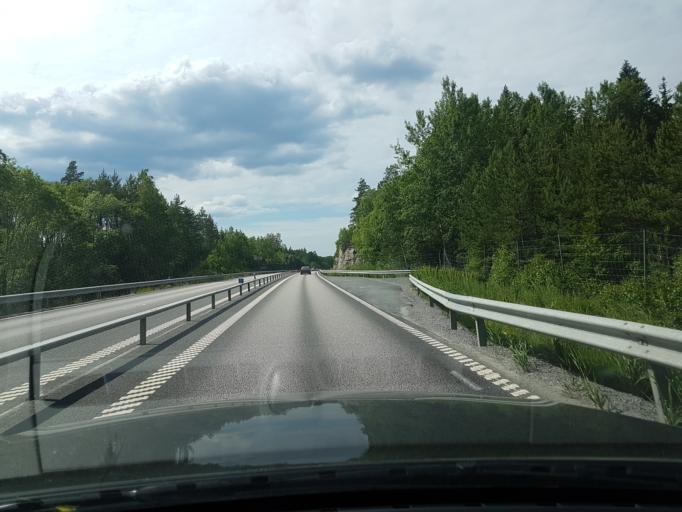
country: SE
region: Stockholm
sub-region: Norrtalje Kommun
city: Norrtalje
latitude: 59.7290
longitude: 18.8114
